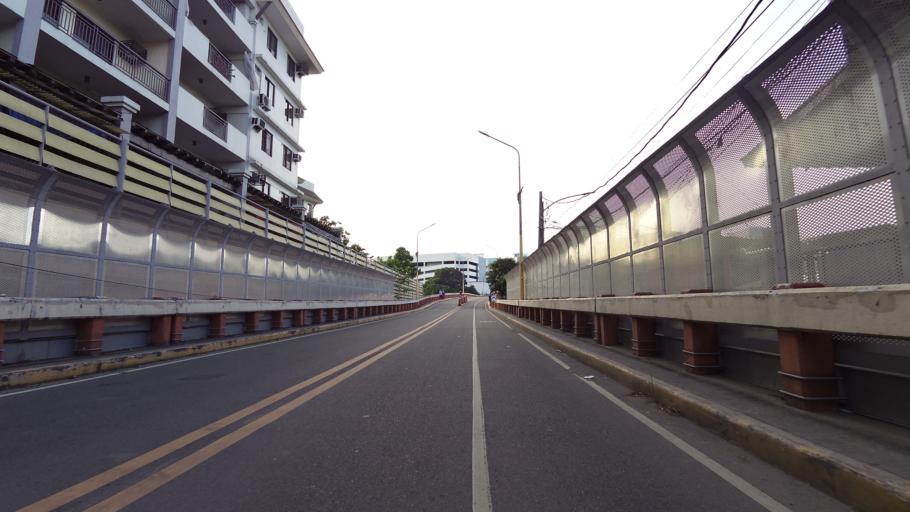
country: PH
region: Metro Manila
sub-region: Pasig
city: Pasig City
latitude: 14.5741
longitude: 121.0775
